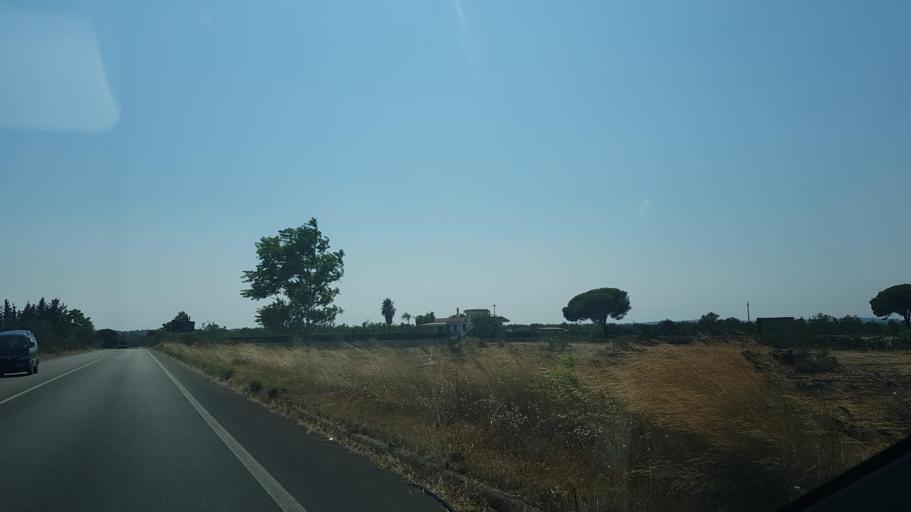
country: IT
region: Apulia
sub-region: Provincia di Lecce
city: Ugento
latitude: 39.9413
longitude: 18.1802
